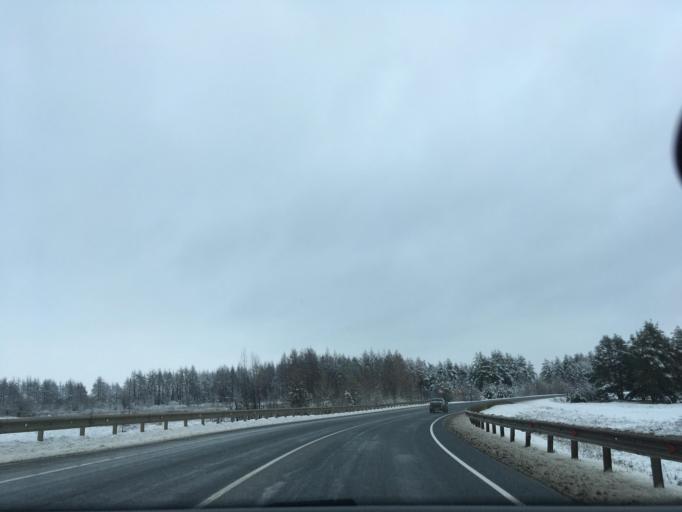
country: RU
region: Voronezj
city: Zabolotovka
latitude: 50.2449
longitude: 39.3830
